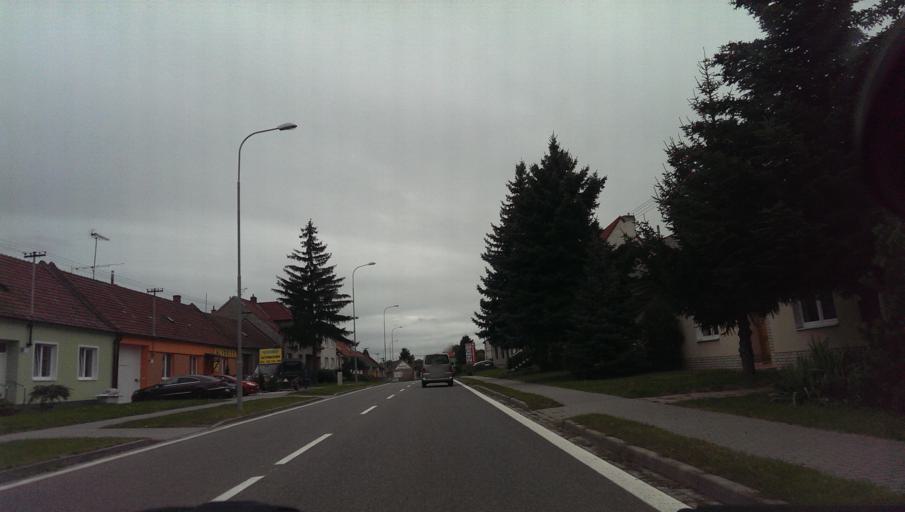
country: CZ
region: South Moravian
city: Bzenec
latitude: 48.9737
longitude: 17.2587
